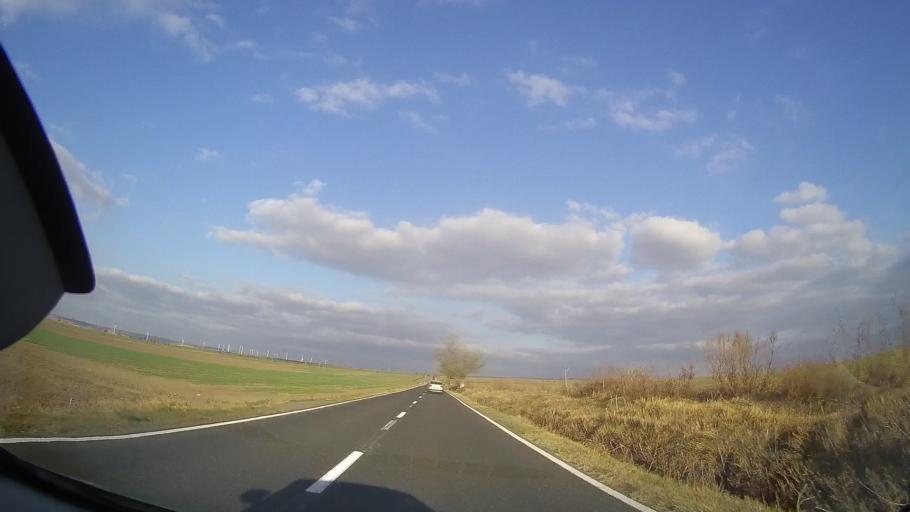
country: RO
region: Tulcea
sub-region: Comuna Topolog
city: Topolog
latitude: 44.8405
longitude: 28.3041
